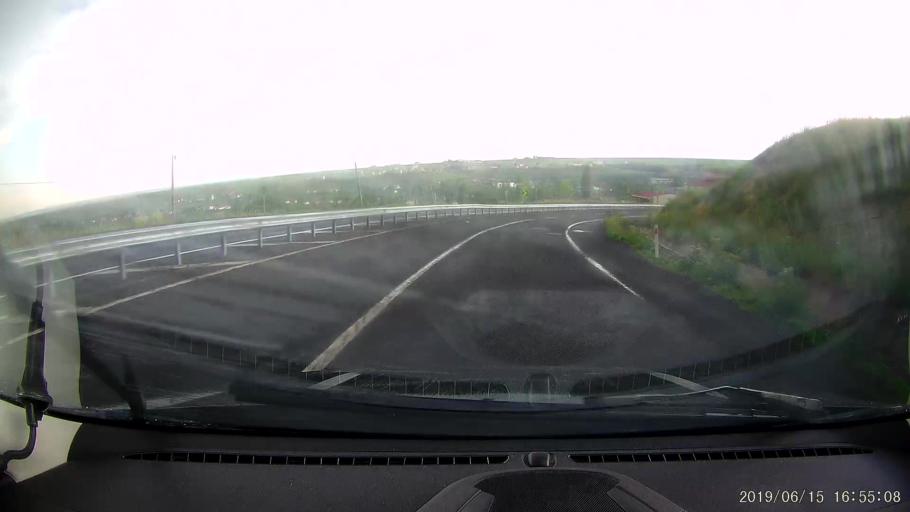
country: TR
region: Kars
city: Susuz
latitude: 40.7857
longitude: 43.1365
